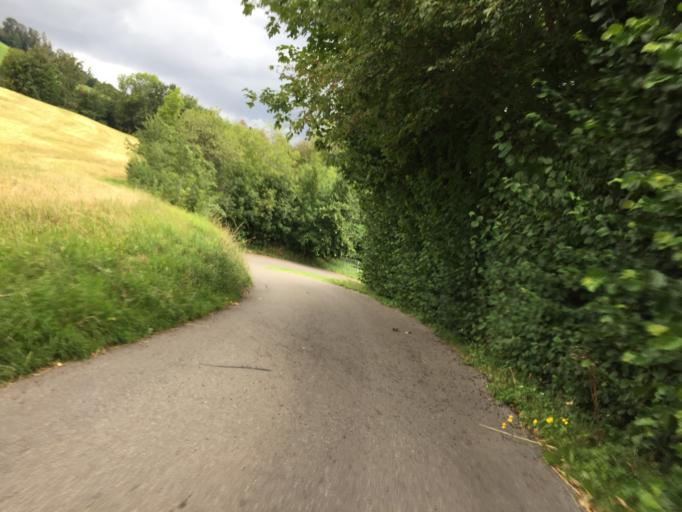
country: CH
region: Bern
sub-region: Bern-Mittelland District
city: Munsingen
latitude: 46.8637
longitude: 7.5447
